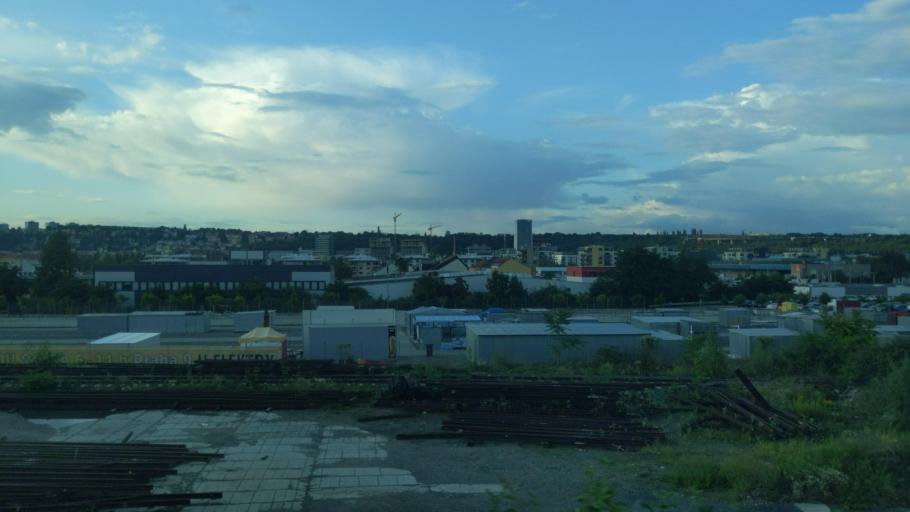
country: CZ
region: Praha
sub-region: Praha 9
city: Vysocany
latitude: 50.1009
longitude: 14.5158
